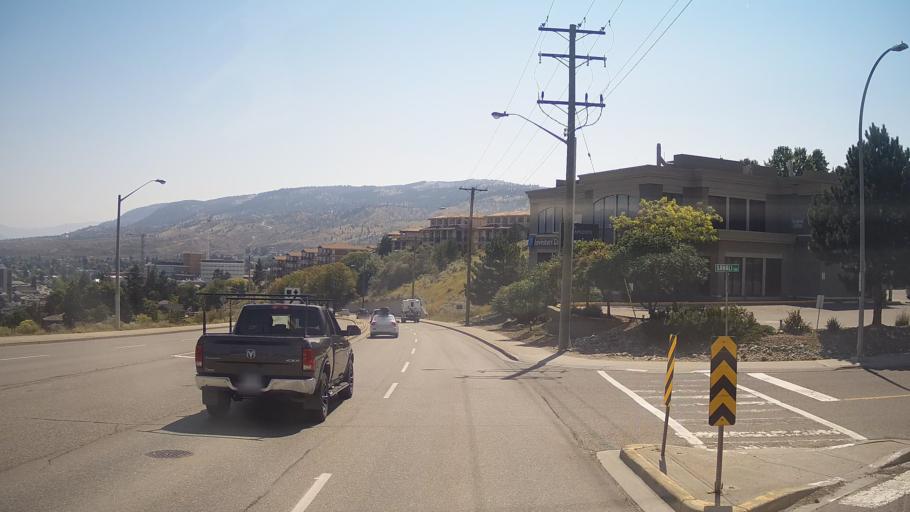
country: CA
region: British Columbia
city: Kamloops
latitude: 50.6725
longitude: -120.3451
